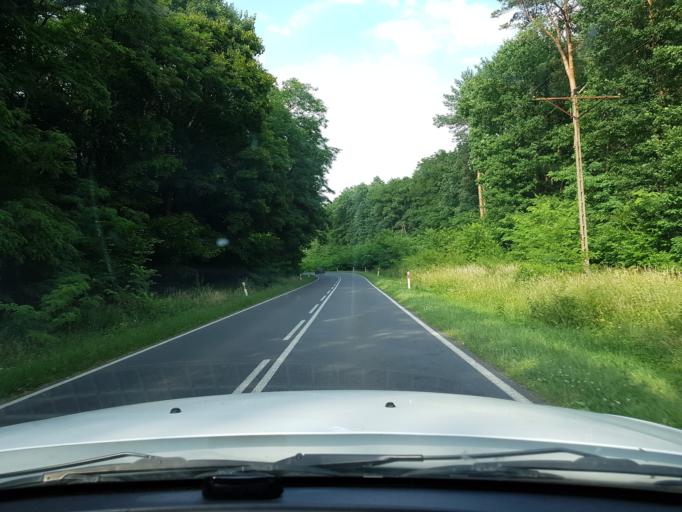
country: PL
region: West Pomeranian Voivodeship
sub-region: Powiat gryfinski
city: Chojna
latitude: 52.9263
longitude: 14.3716
